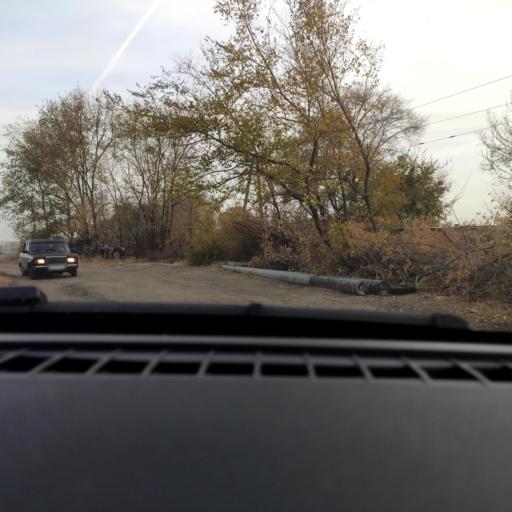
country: RU
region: Voronezj
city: Voronezh
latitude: 51.6594
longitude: 39.2683
